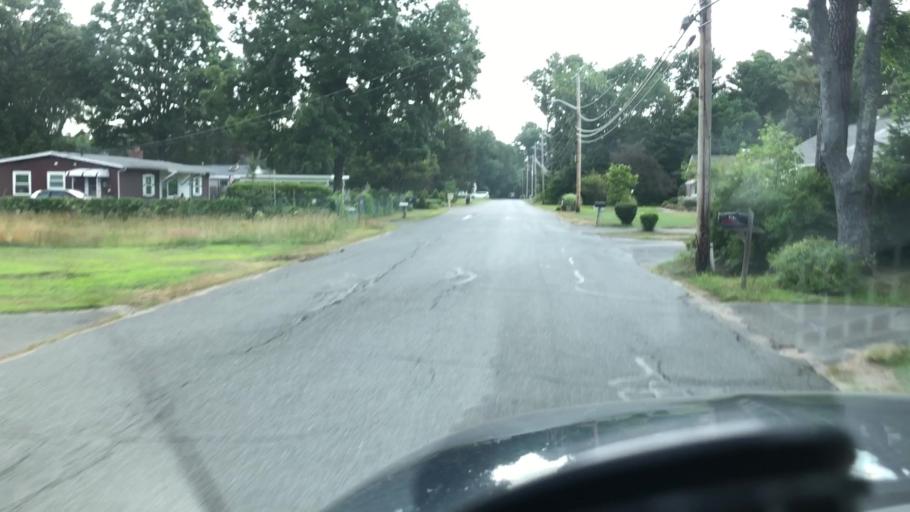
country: US
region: Massachusetts
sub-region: Hampshire County
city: Southampton
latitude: 42.1840
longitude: -72.6823
